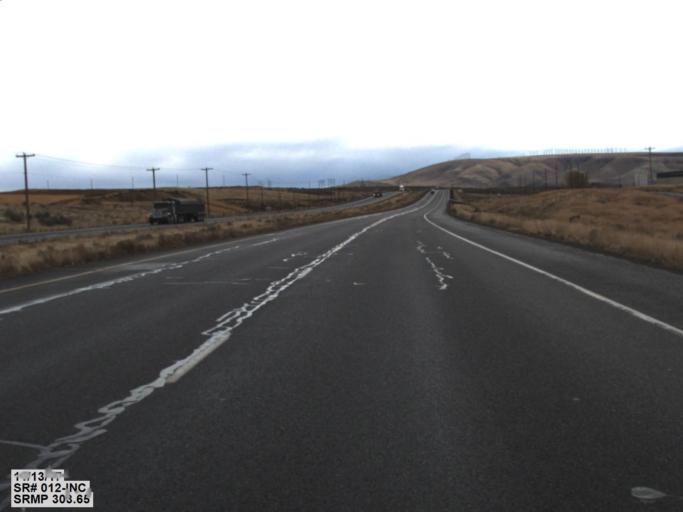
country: US
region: Washington
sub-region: Benton County
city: Finley
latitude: 46.1116
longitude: -118.9199
